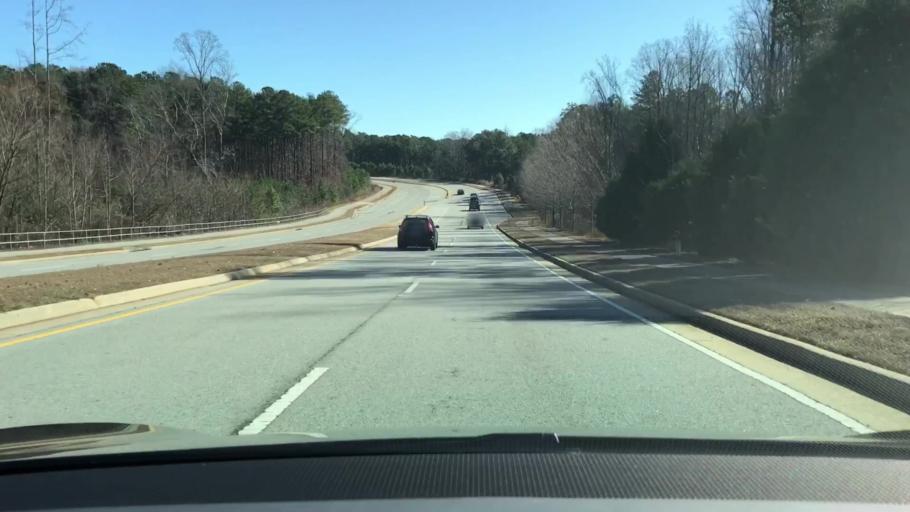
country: US
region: Georgia
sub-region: Gwinnett County
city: Suwanee
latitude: 34.0219
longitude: -84.0497
